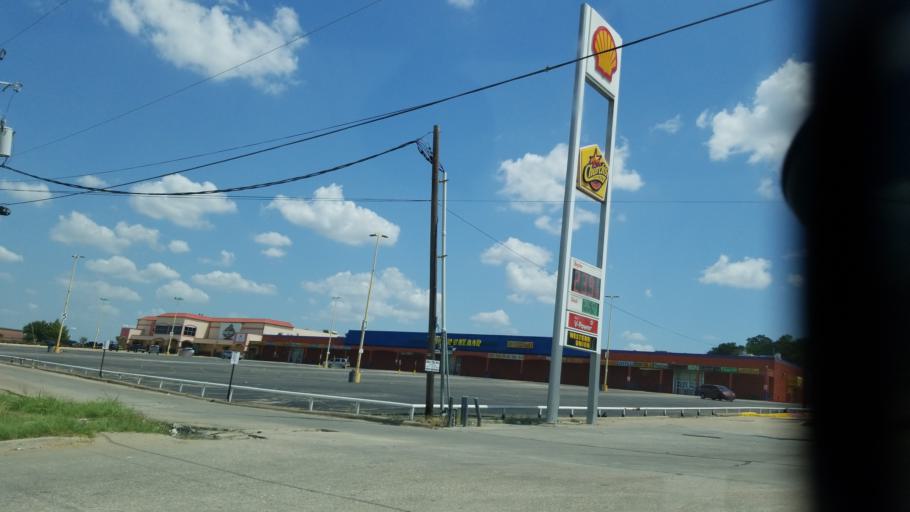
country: US
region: Texas
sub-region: Dallas County
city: Cockrell Hill
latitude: 32.7367
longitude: -96.9186
